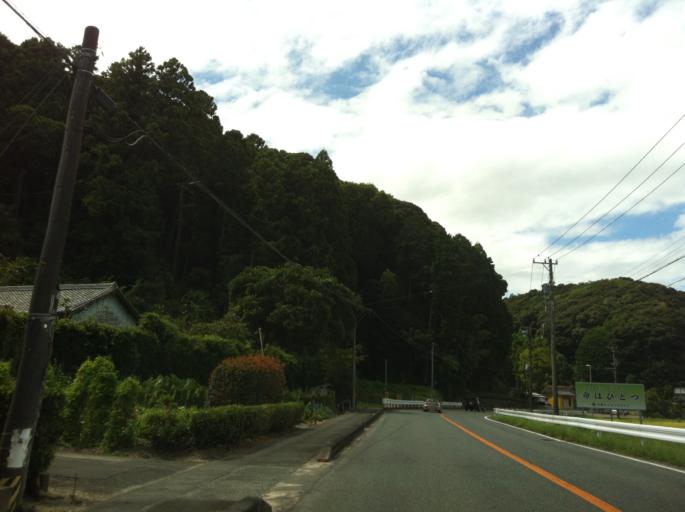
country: JP
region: Shizuoka
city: Kakegawa
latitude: 34.7259
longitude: 138.0457
